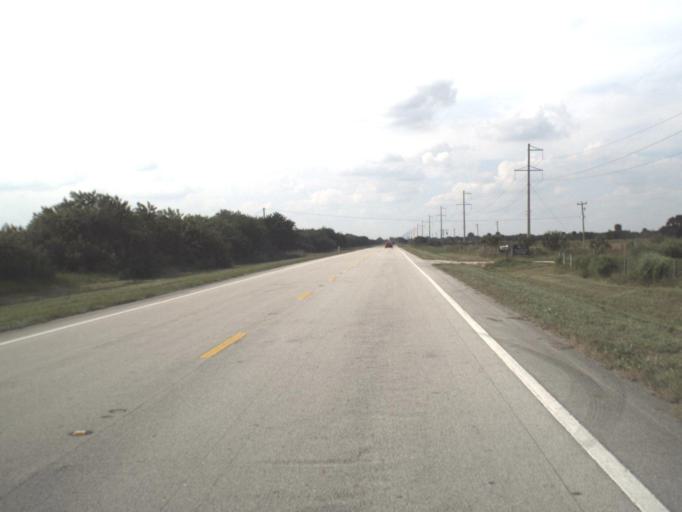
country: US
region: Florida
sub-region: Okeechobee County
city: Taylor Creek
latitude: 27.1846
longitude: -80.7159
